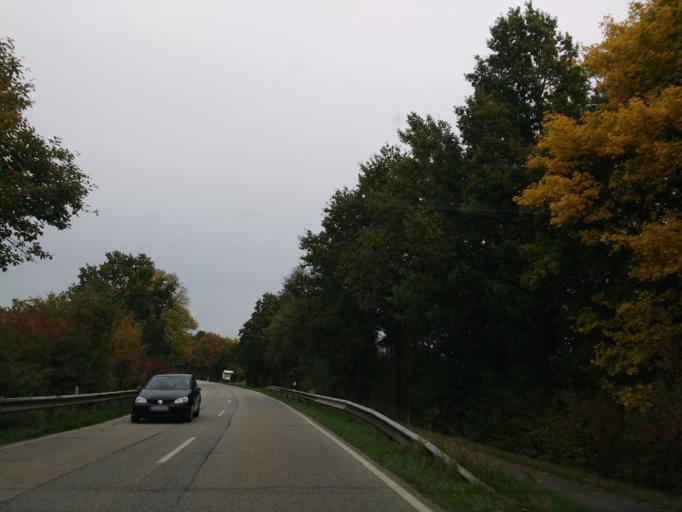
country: DE
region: Schleswig-Holstein
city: Gromitz
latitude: 54.1592
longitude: 10.9637
